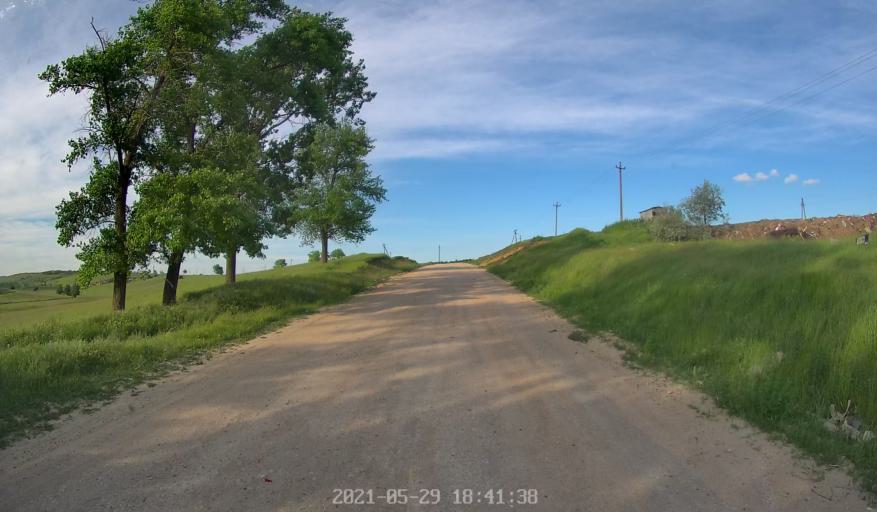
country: MD
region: Chisinau
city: Singera
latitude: 46.8081
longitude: 28.9587
